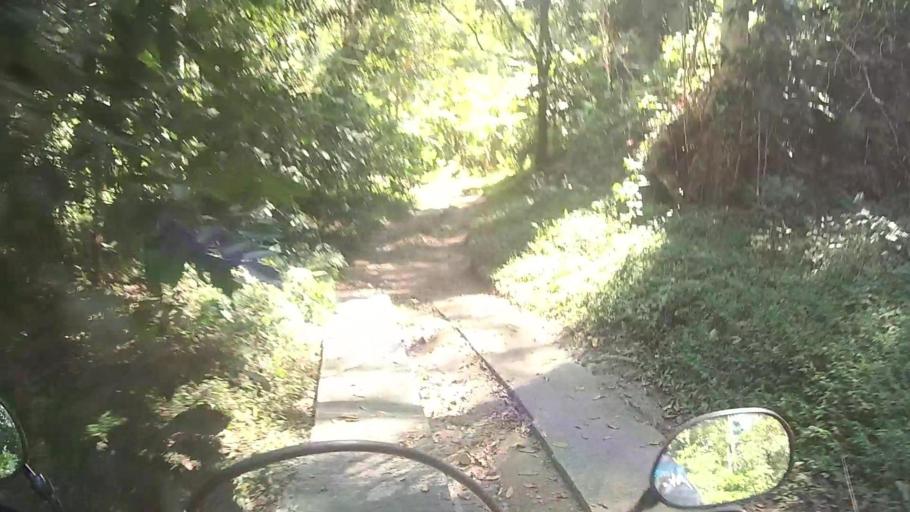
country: TH
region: Chiang Mai
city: Mae On
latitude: 19.0617
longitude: 99.3326
